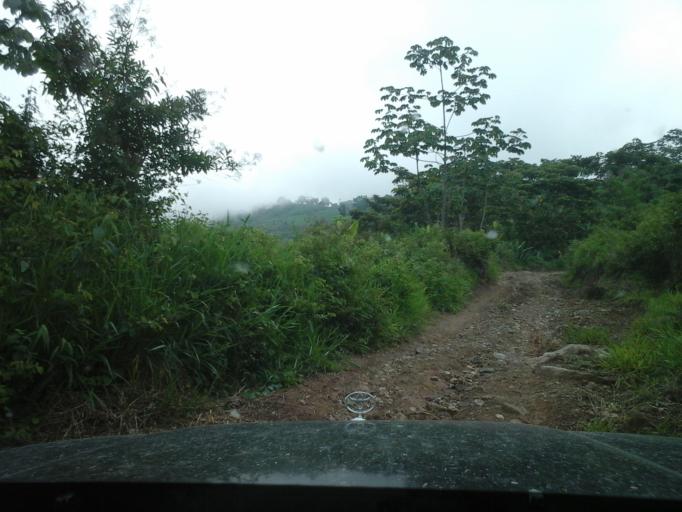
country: CO
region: Cesar
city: Agustin Codazzi
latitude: 9.9540
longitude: -73.0676
